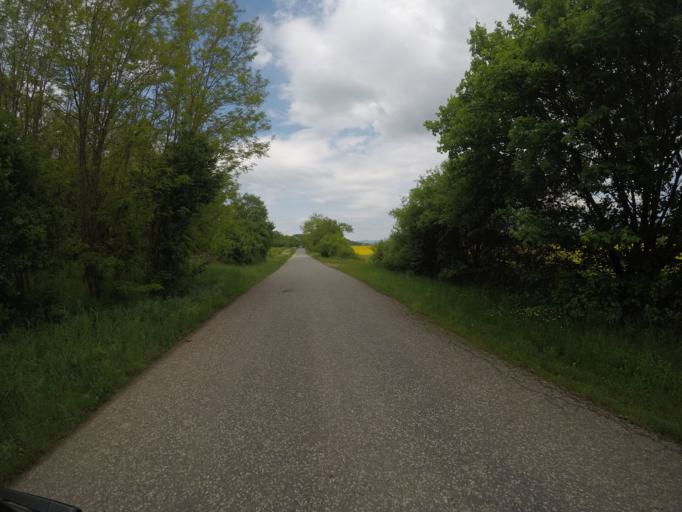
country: SK
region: Banskobystricky
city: Dudince
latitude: 48.0963
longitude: 18.8709
